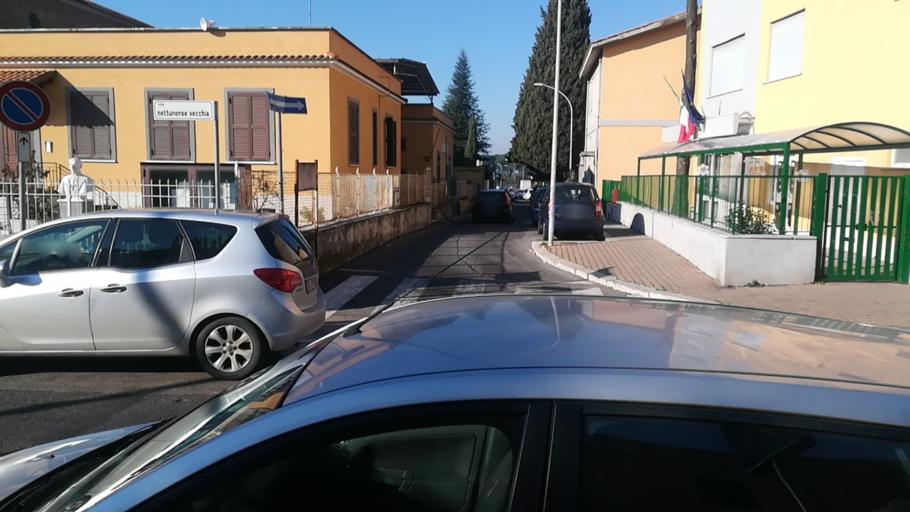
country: IT
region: Latium
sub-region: Citta metropolitana di Roma Capitale
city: Marino
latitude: 41.7639
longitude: 12.6183
